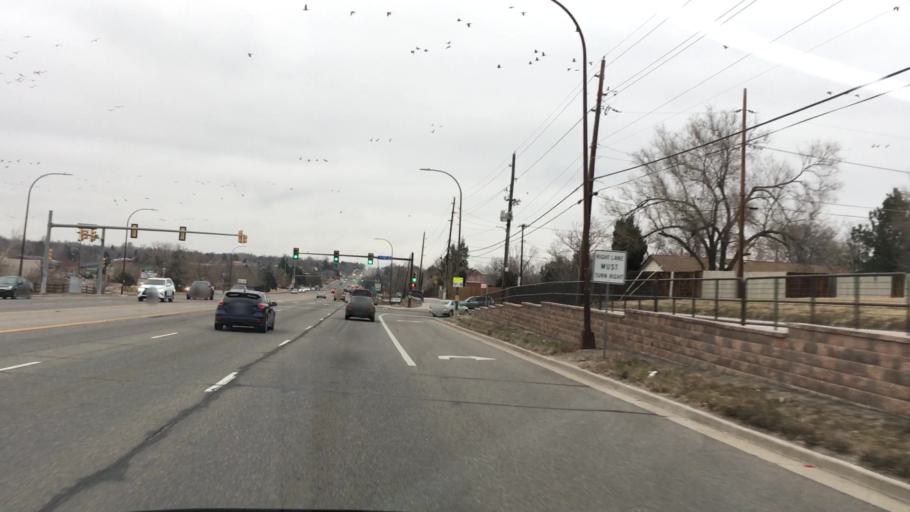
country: US
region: Colorado
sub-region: Jefferson County
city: Arvada
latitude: 39.8342
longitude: -105.0816
